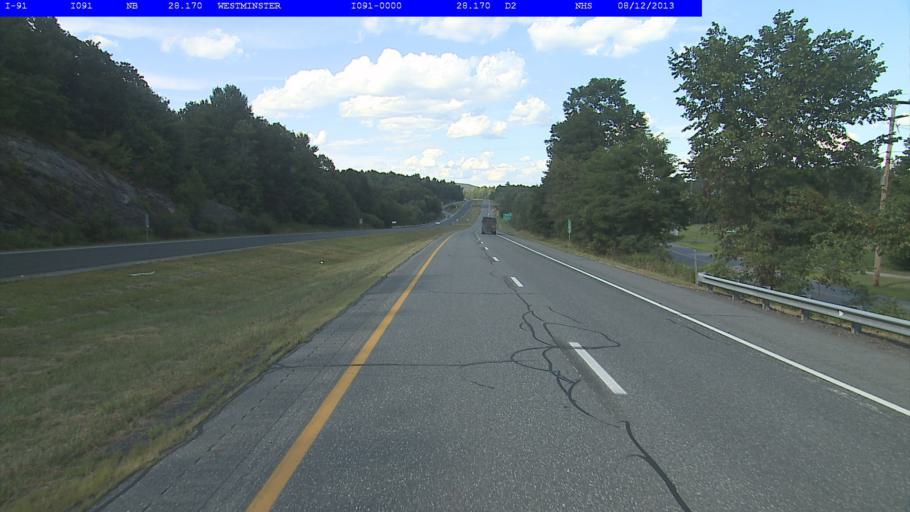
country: US
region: Vermont
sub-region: Windham County
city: Bellows Falls
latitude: 43.0854
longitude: -72.4603
